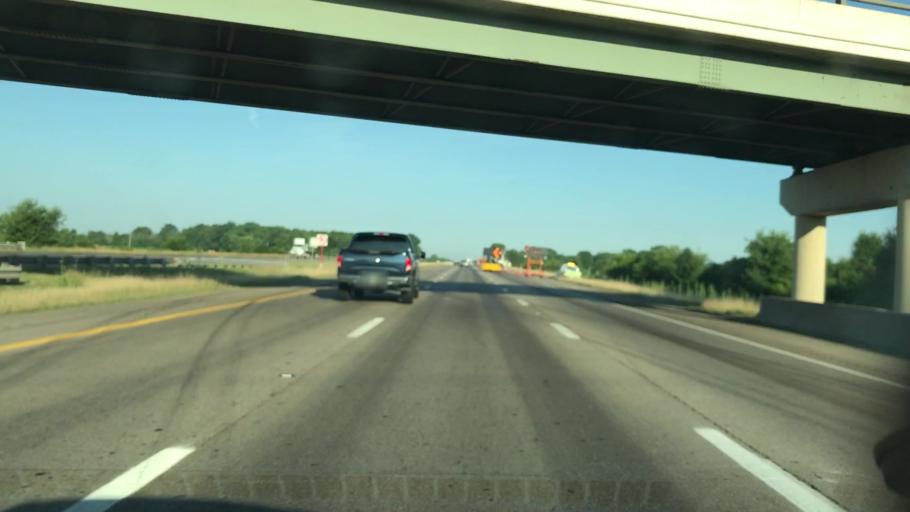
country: US
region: Ohio
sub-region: Franklin County
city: Lake Darby
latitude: 39.9799
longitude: -83.2001
